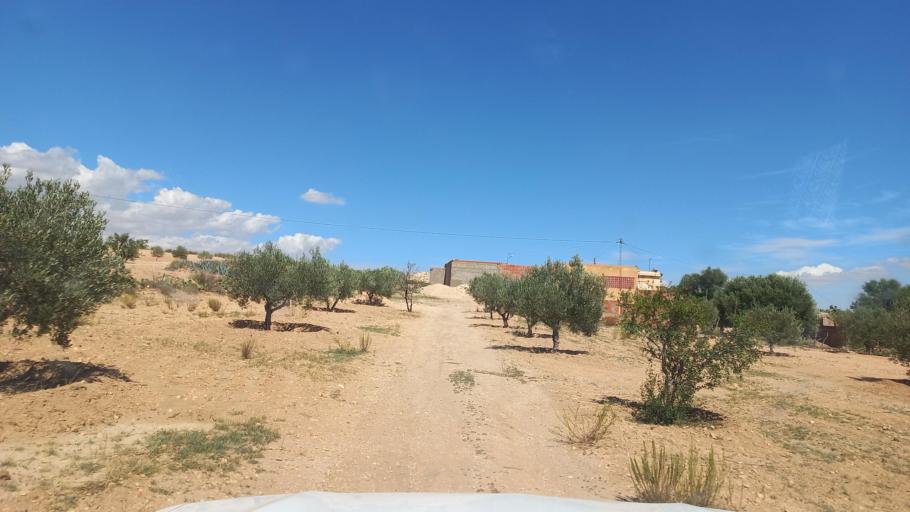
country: TN
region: Al Qasrayn
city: Sbiba
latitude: 35.3531
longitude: 9.0079
